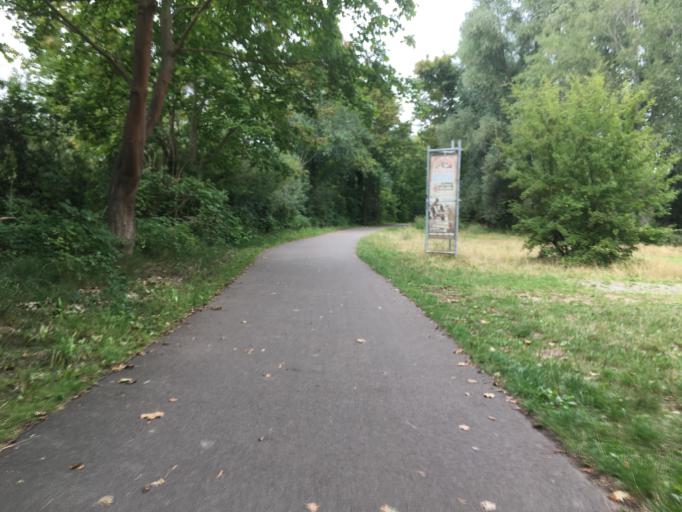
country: DE
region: Brandenburg
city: Prenzlau
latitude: 53.2995
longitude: 13.8459
